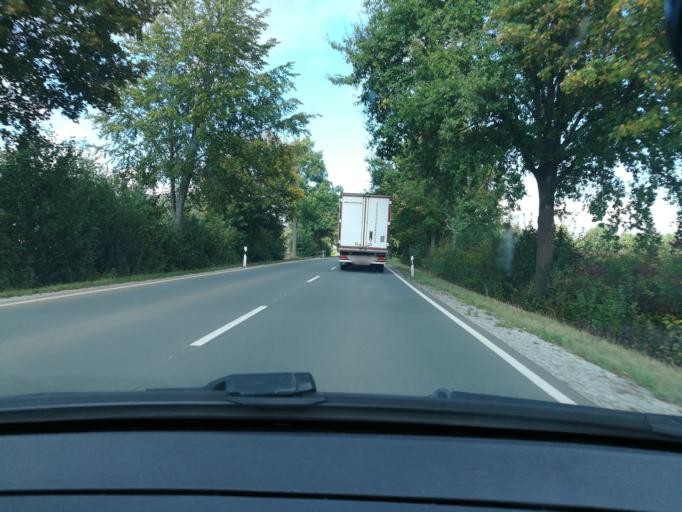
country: DE
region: North Rhine-Westphalia
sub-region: Regierungsbezirk Munster
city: Beelen
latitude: 51.9448
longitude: 8.1243
